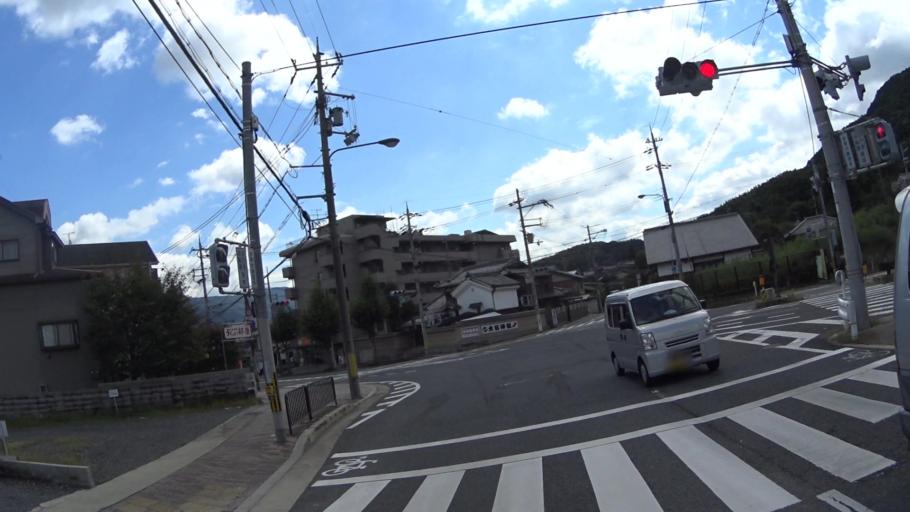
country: JP
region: Kyoto
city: Kyoto
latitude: 34.9717
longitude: 135.7969
